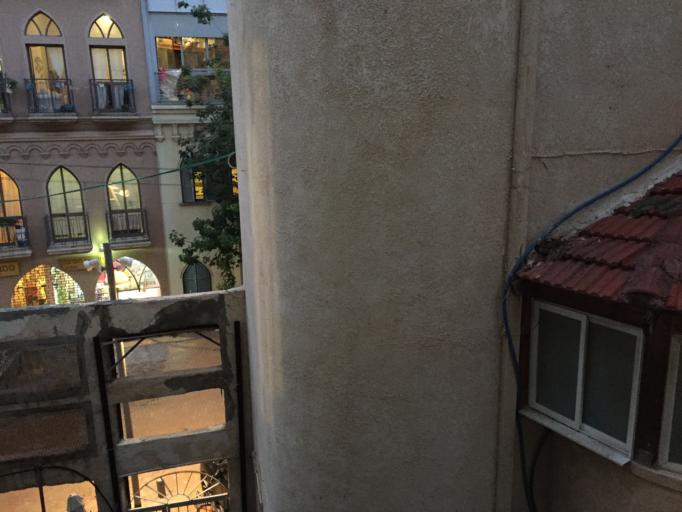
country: IL
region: Tel Aviv
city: Tel Aviv
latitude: 32.0685
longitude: 34.7697
